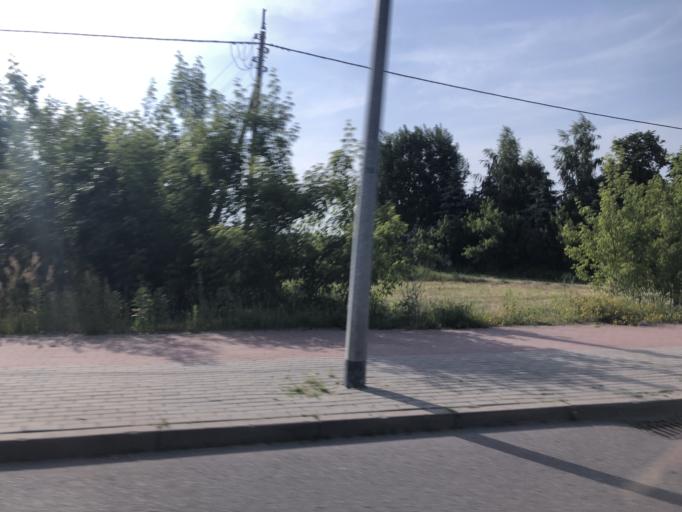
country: PL
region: Podlasie
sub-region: Lomza
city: Lomza
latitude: 53.1583
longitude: 22.0312
